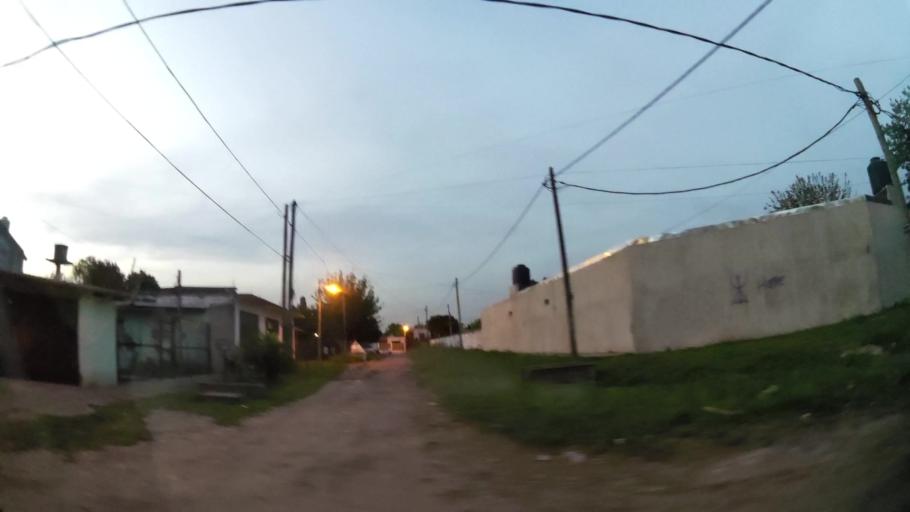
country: AR
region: Buenos Aires
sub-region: Partido de Quilmes
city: Quilmes
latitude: -34.8039
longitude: -58.2921
